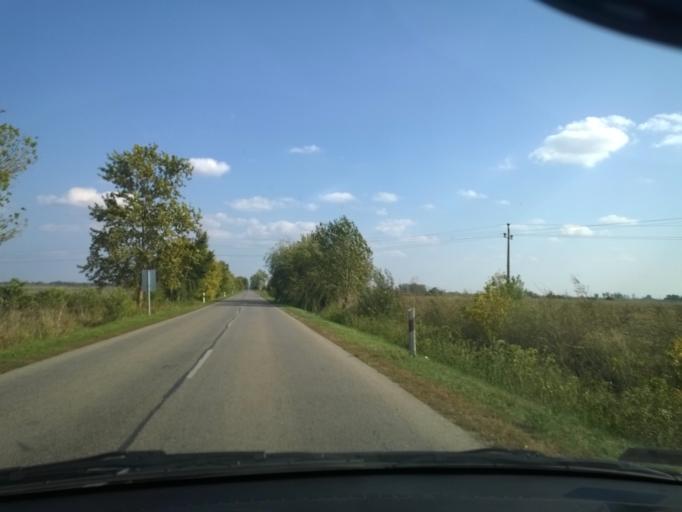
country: HU
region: Bacs-Kiskun
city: Kalocsa
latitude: 46.5118
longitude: 19.0110
